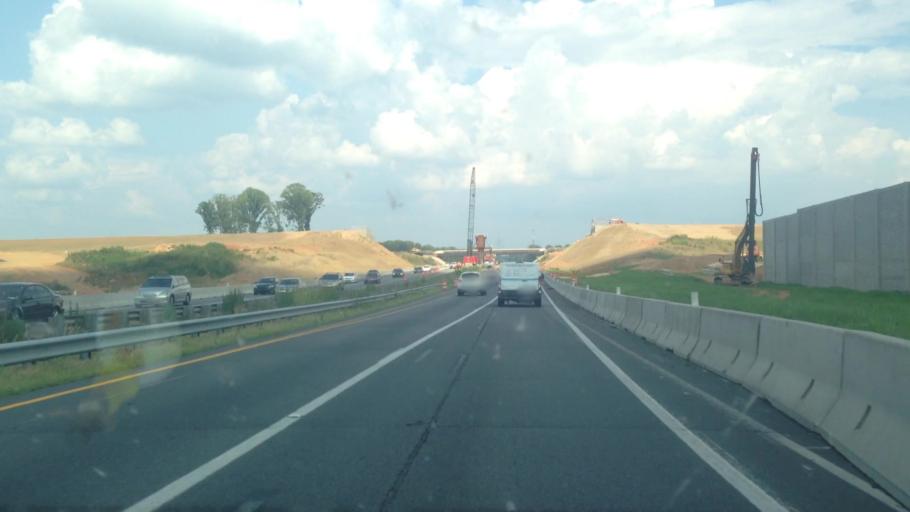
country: US
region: North Carolina
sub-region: Forsyth County
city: Kernersville
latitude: 36.1131
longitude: -80.1362
